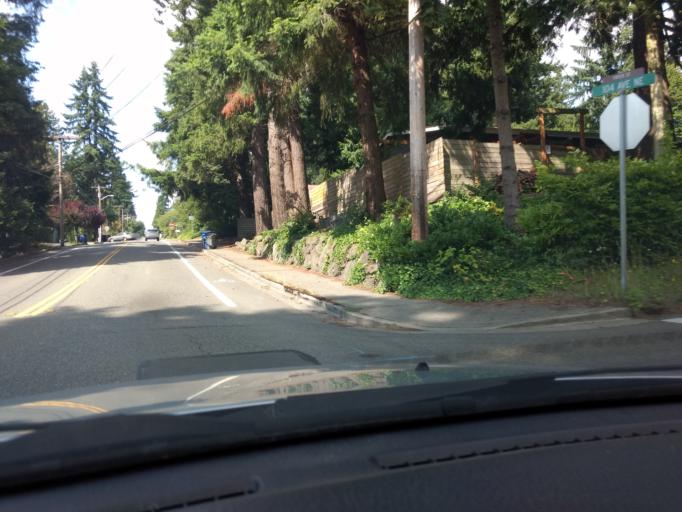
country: US
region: Washington
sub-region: King County
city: Bothell
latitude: 47.7650
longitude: -122.2056
